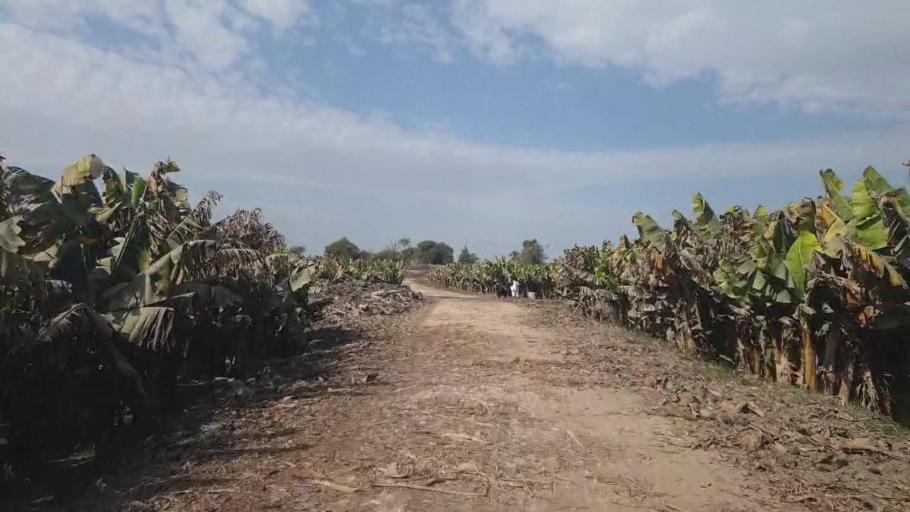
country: PK
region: Sindh
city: Sakrand
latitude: 25.9883
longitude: 68.3280
